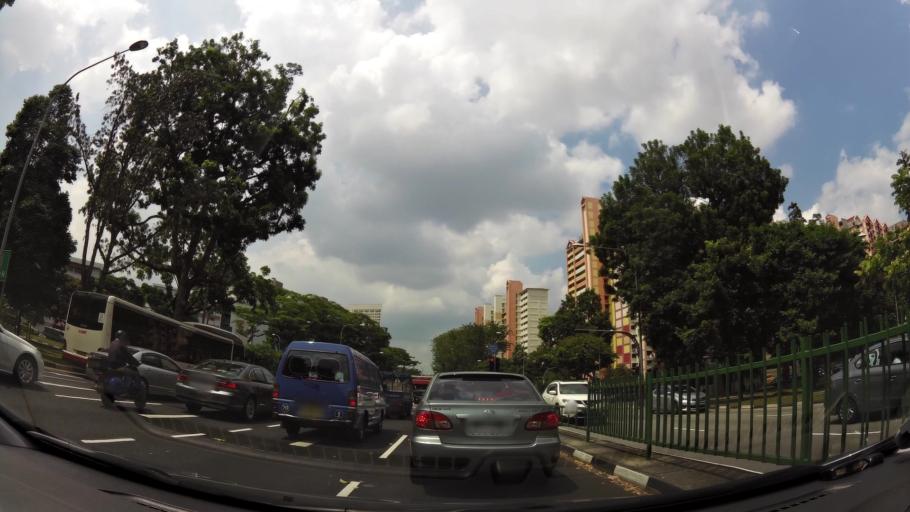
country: SG
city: Singapore
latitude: 1.2817
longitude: 103.8242
